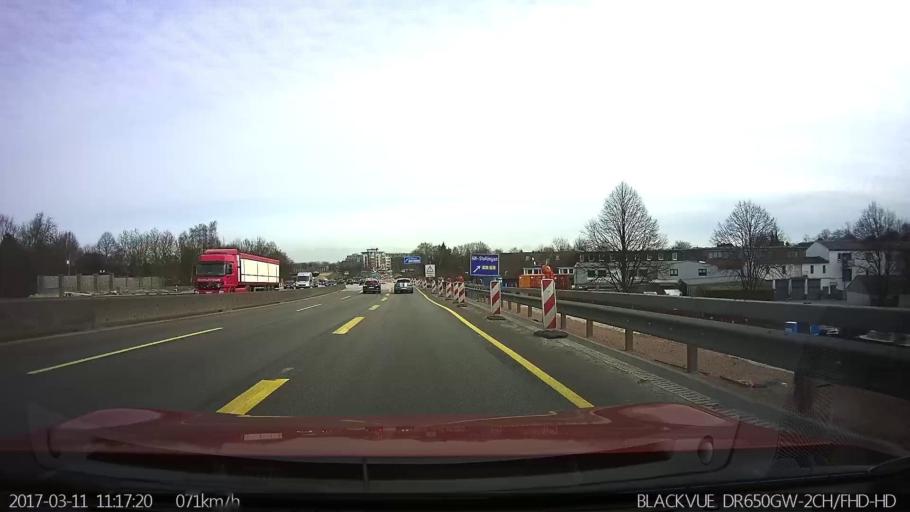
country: DE
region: Hamburg
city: Stellingen
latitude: 53.5915
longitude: 9.9190
